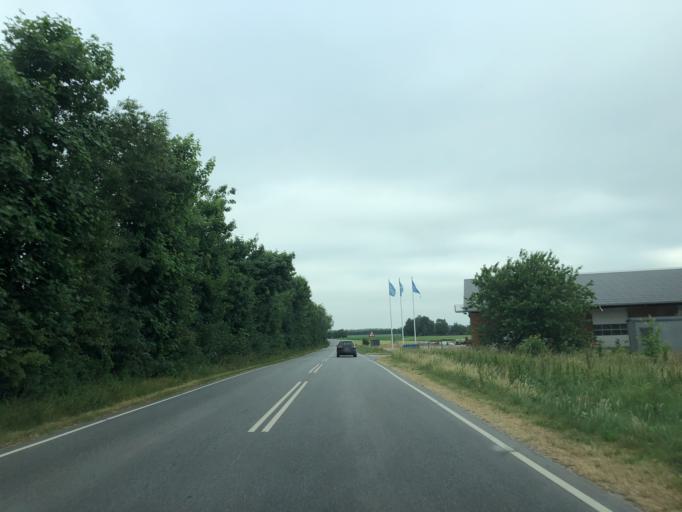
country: DK
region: Central Jutland
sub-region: Holstebro Kommune
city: Holstebro
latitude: 56.2681
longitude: 8.6444
